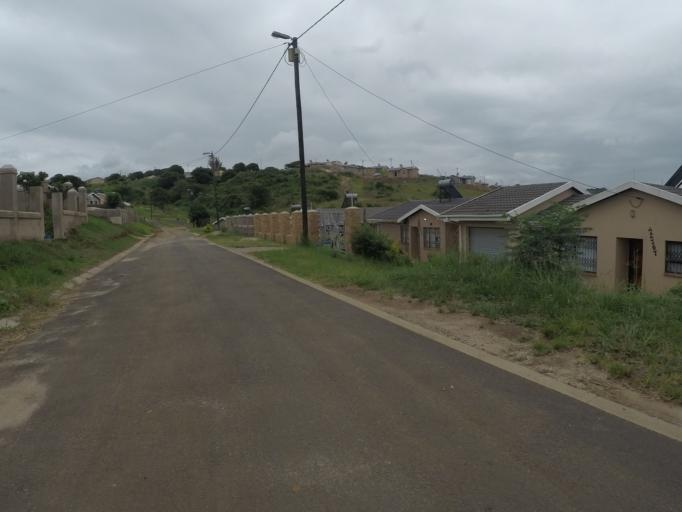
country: ZA
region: KwaZulu-Natal
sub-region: uThungulu District Municipality
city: Empangeni
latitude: -28.7703
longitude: 31.8732
